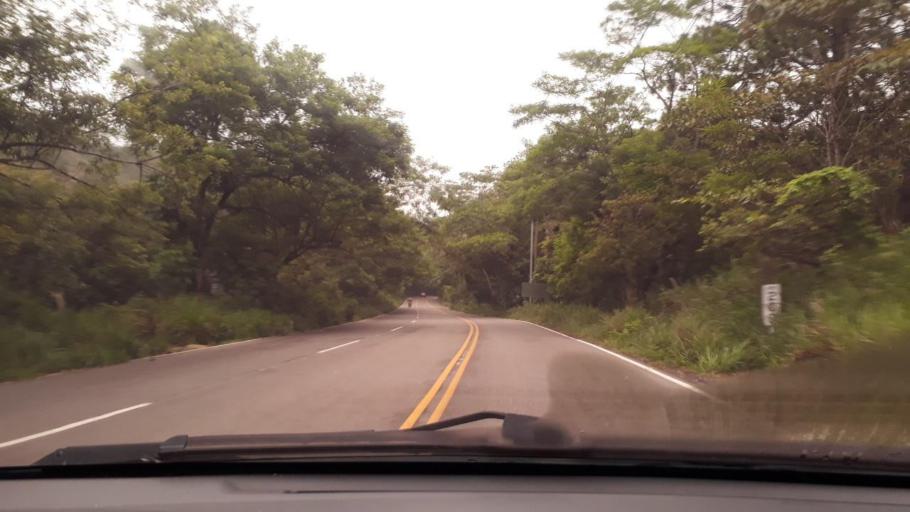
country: GT
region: Chiquimula
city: Concepcion Las Minas
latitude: 14.5552
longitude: -89.4434
